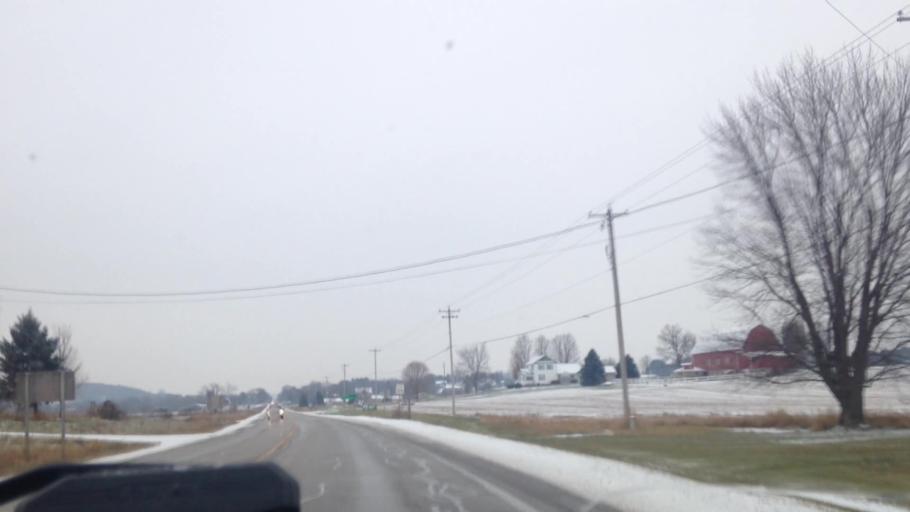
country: US
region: Wisconsin
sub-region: Dodge County
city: Hustisford
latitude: 43.3257
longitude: -88.5183
